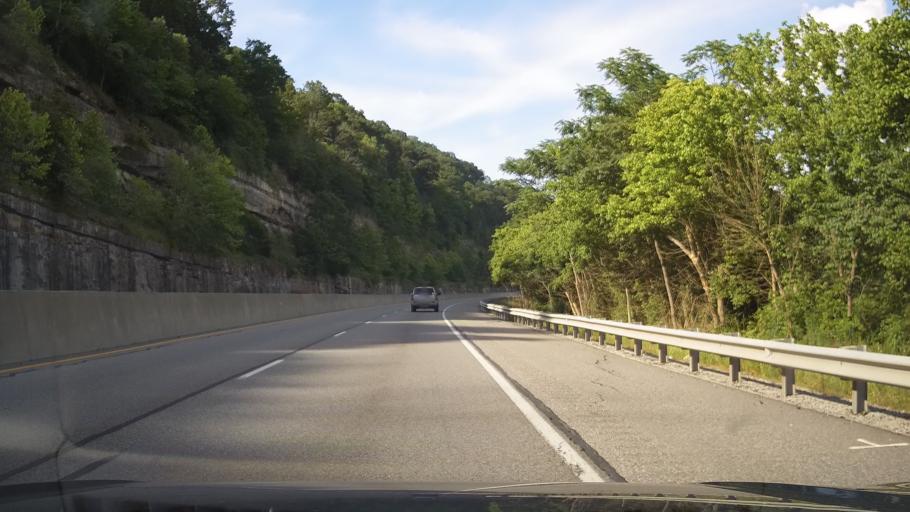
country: US
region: Kentucky
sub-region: Lawrence County
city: Louisa
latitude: 37.9832
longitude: -82.6708
